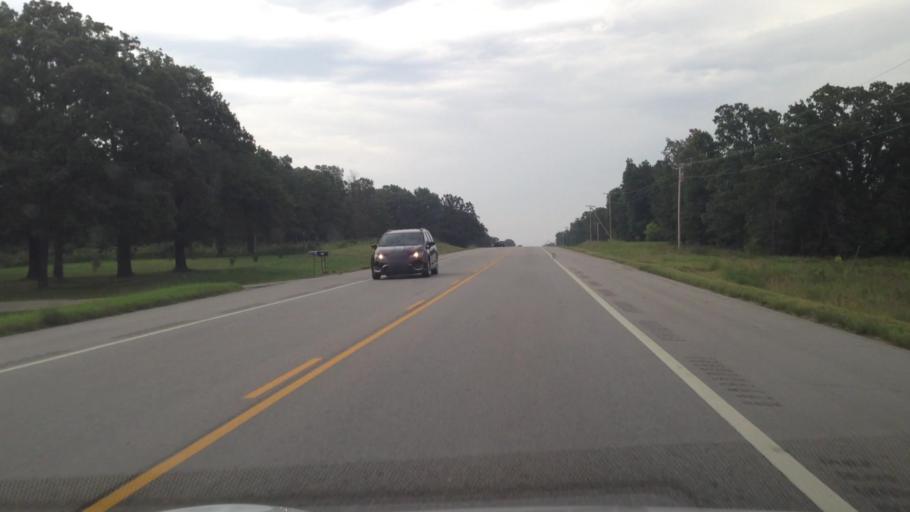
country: US
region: Kansas
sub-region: Cherokee County
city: Galena
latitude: 37.0237
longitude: -94.6641
